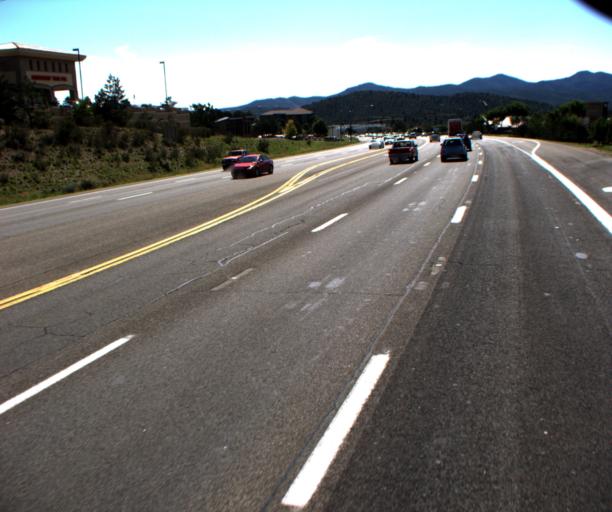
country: US
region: Arizona
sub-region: Yavapai County
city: Prescott
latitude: 34.5498
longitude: -112.4062
